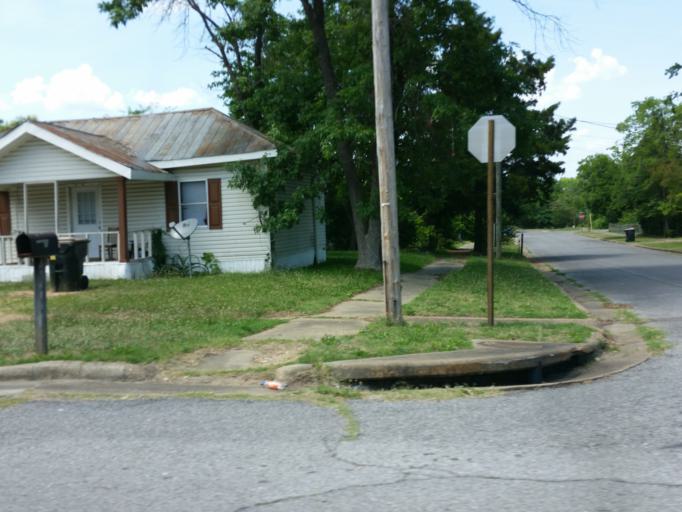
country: US
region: Alabama
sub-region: Marengo County
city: Demopolis
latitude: 32.5184
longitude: -87.8328
